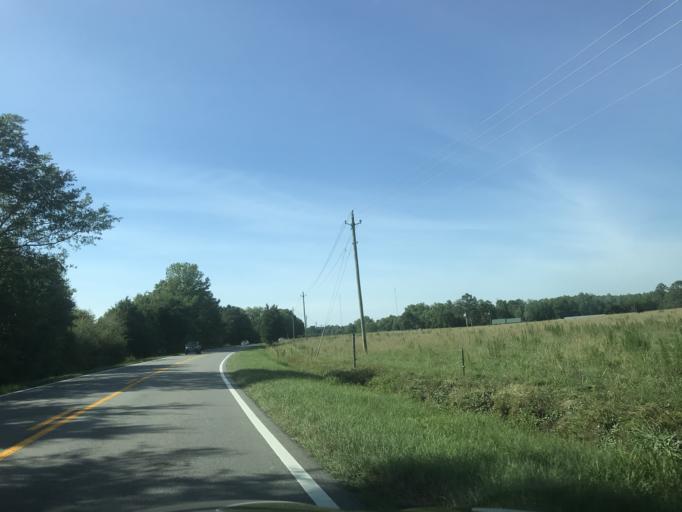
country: US
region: North Carolina
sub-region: Johnston County
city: Clayton
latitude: 35.6111
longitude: -78.5353
